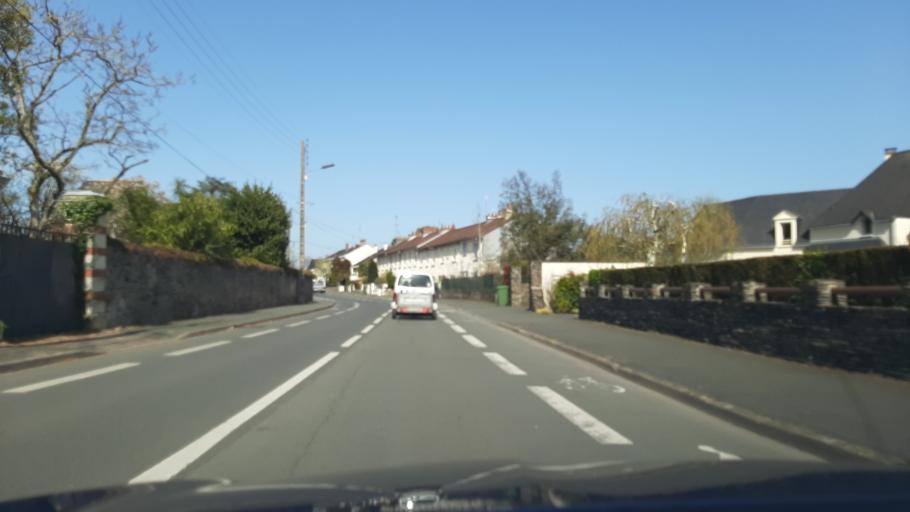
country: FR
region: Pays de la Loire
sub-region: Departement de Maine-et-Loire
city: Les Ponts-de-Ce
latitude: 47.4460
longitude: -0.5264
